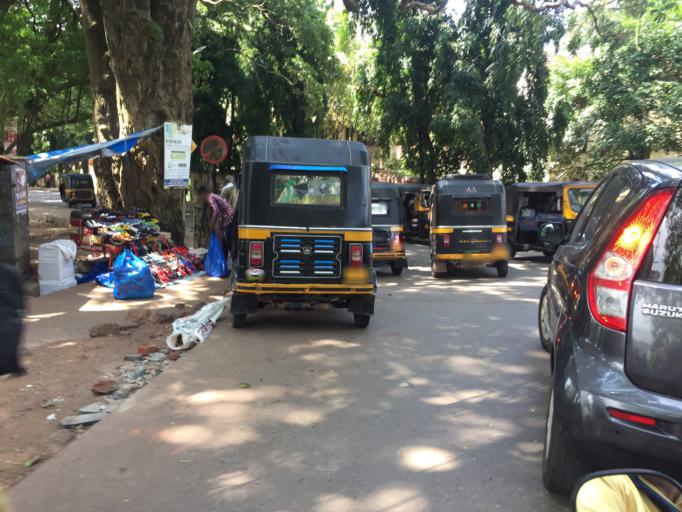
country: IN
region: Karnataka
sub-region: Dakshina Kannada
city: Mangalore
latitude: 12.8656
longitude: 74.8433
